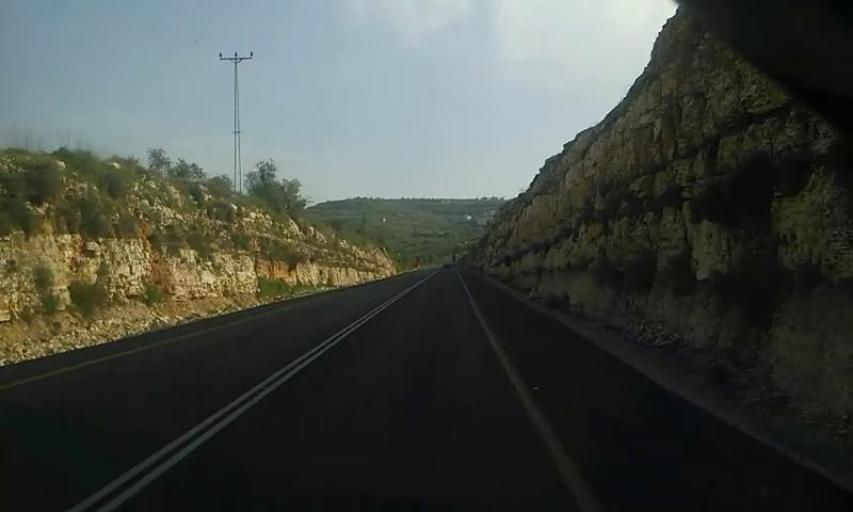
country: PS
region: West Bank
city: Jit
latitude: 32.2178
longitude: 35.1751
